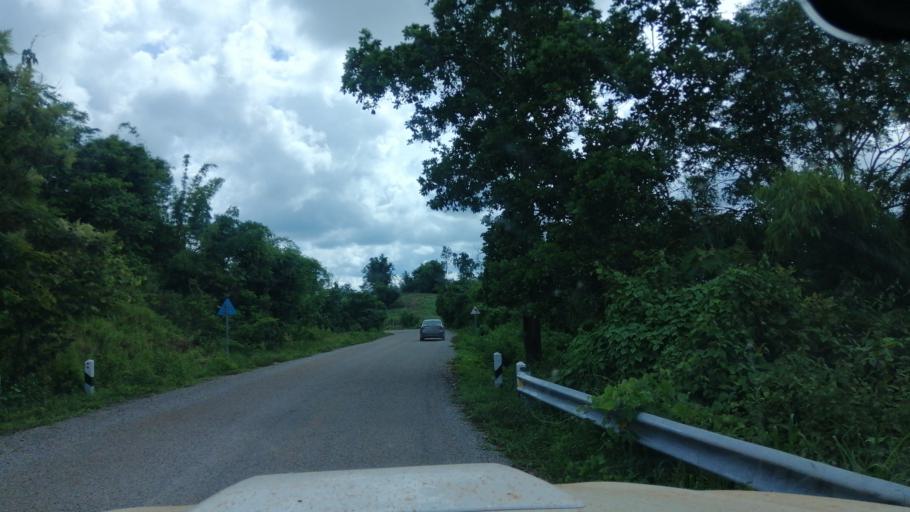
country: TH
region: Uttaradit
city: Ban Khok
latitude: 18.3756
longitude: 101.1482
